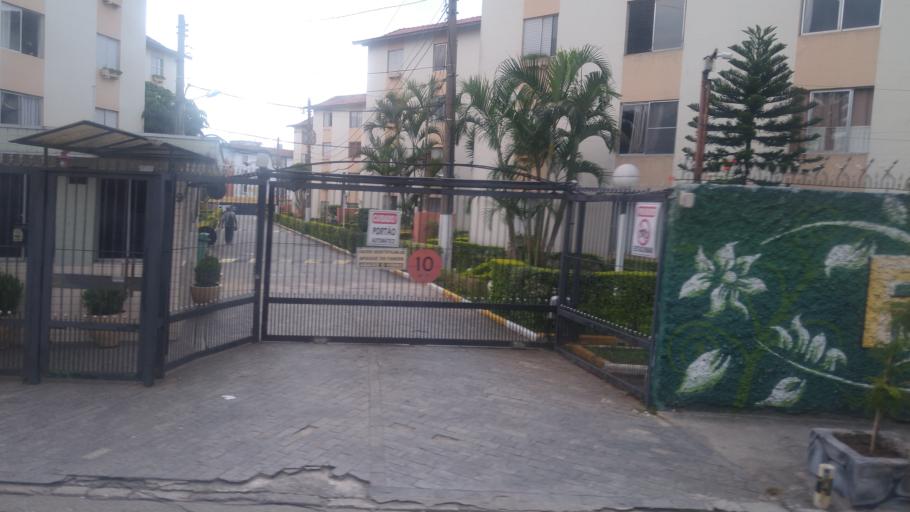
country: BR
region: Sao Paulo
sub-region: Sao Paulo
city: Sao Paulo
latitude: -23.4660
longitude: -46.6686
